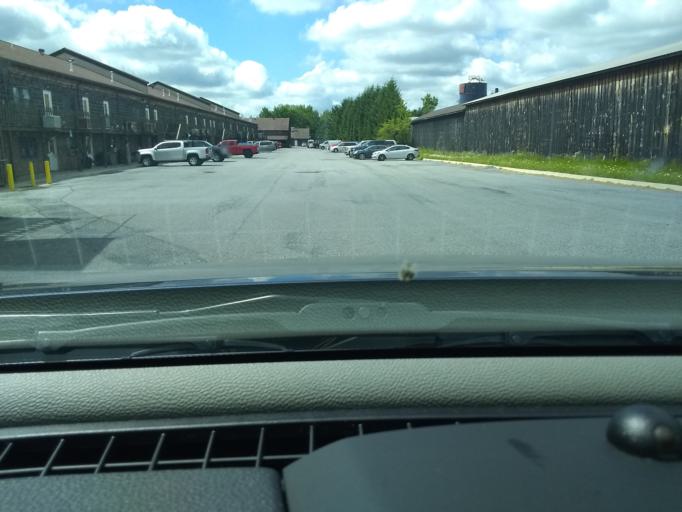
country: US
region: Pennsylvania
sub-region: Cambria County
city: Ebensburg
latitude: 40.4628
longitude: -78.7515
